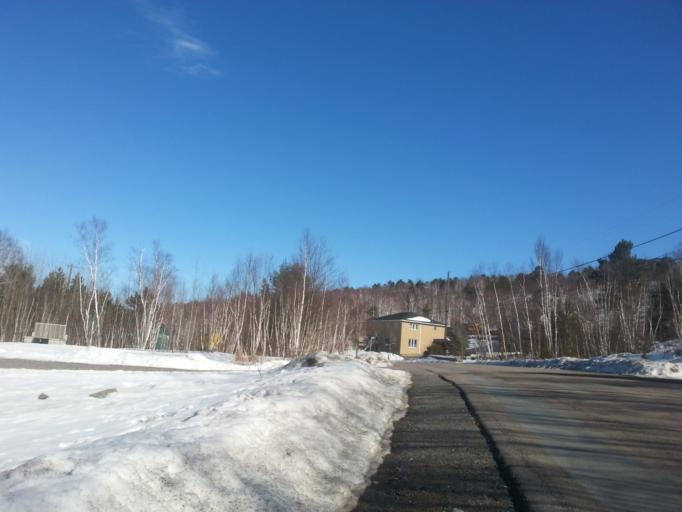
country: CA
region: Ontario
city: Greater Sudbury
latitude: 46.4037
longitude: -81.0275
